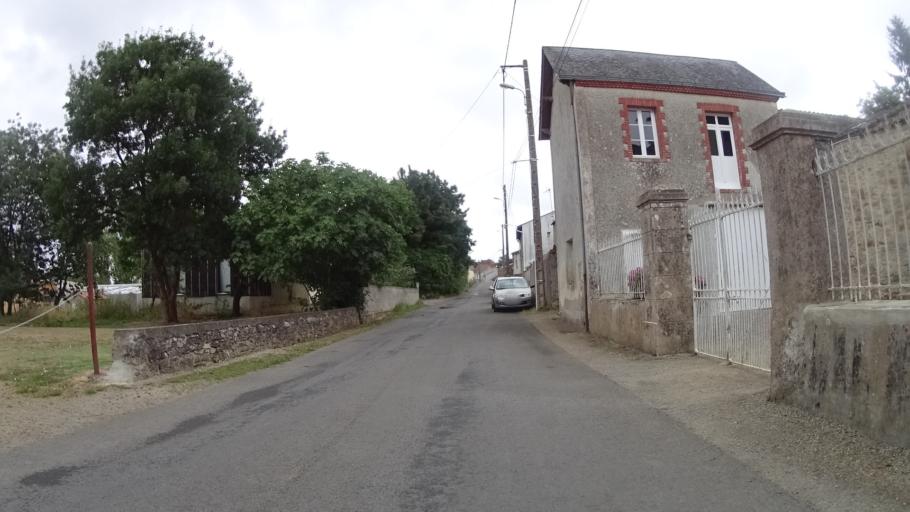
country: FR
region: Pays de la Loire
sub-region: Departement de la Loire-Atlantique
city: Le Pellerin
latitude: 47.2059
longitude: -1.7812
